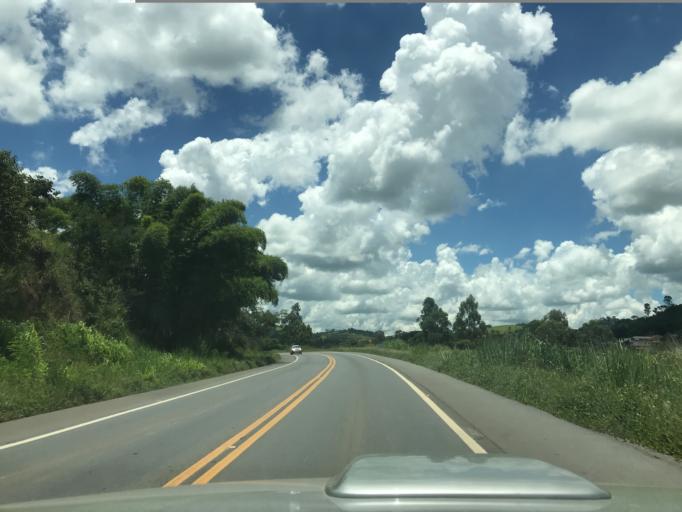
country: BR
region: Minas Gerais
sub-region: Perdoes
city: Perdoes
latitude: -21.0915
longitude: -45.0992
